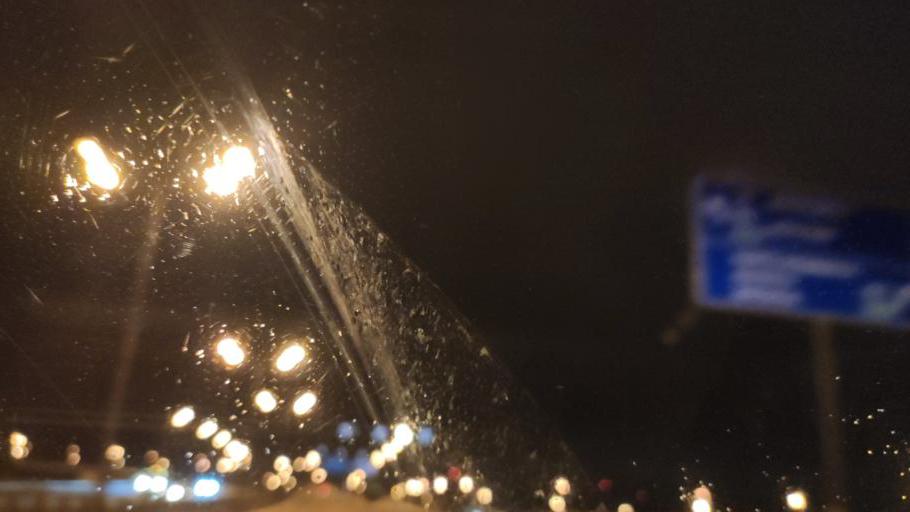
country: RU
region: Moscow
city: Vnukovo
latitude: 55.5780
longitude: 37.2072
